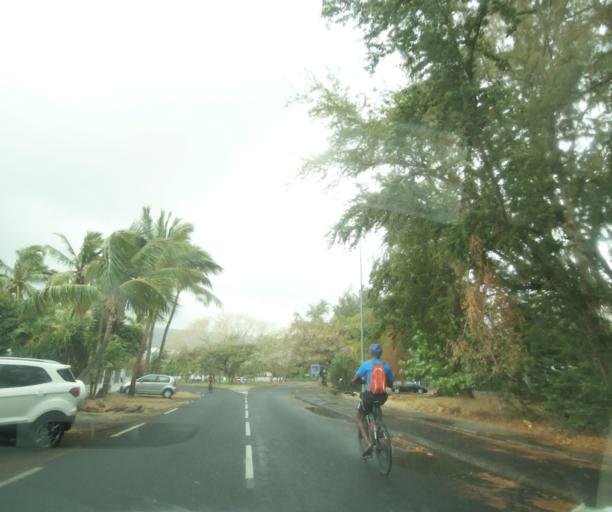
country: RE
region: Reunion
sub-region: Reunion
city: Saint-Paul
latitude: -20.9905
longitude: 55.2826
